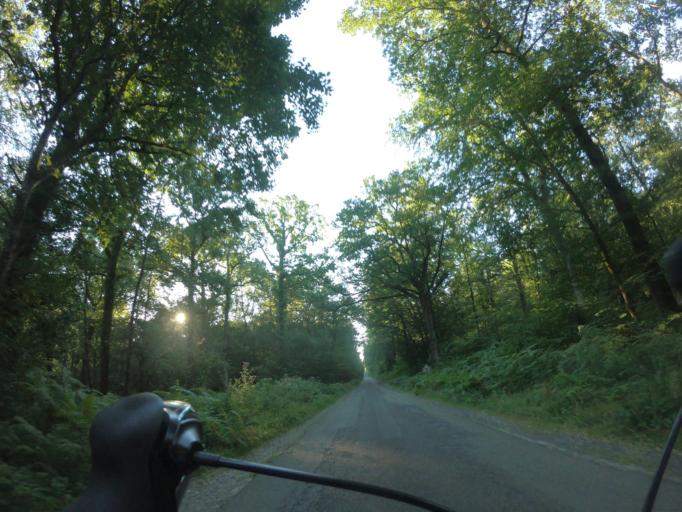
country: FR
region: Lower Normandy
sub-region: Departement de l'Orne
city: Magny-le-Desert
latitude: 48.5390
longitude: -0.3291
